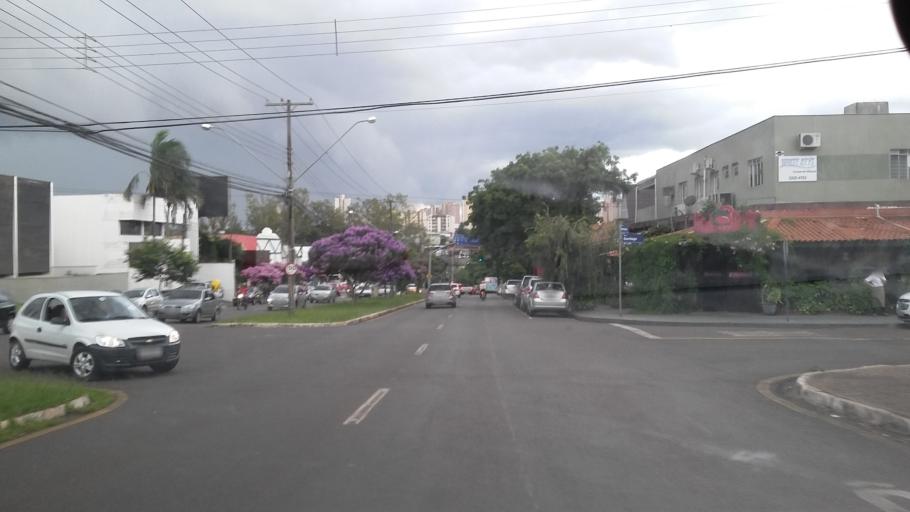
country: BR
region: Parana
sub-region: Londrina
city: Londrina
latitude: -23.3331
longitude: -51.1676
